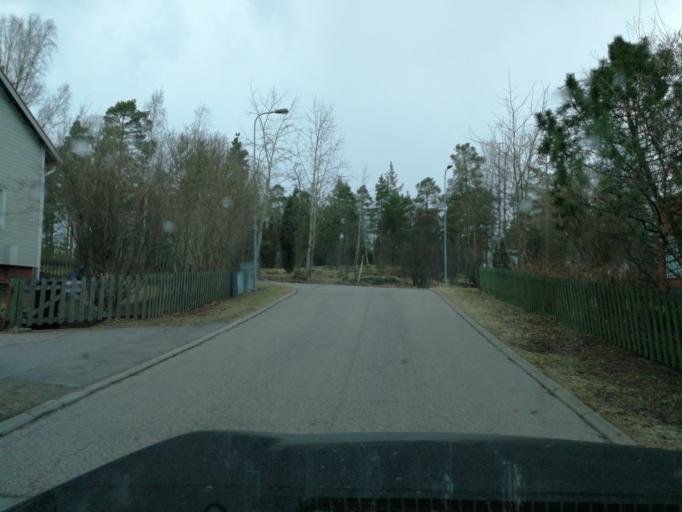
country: FI
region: Uusimaa
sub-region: Helsinki
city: Teekkarikylae
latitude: 60.2426
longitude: 24.8360
